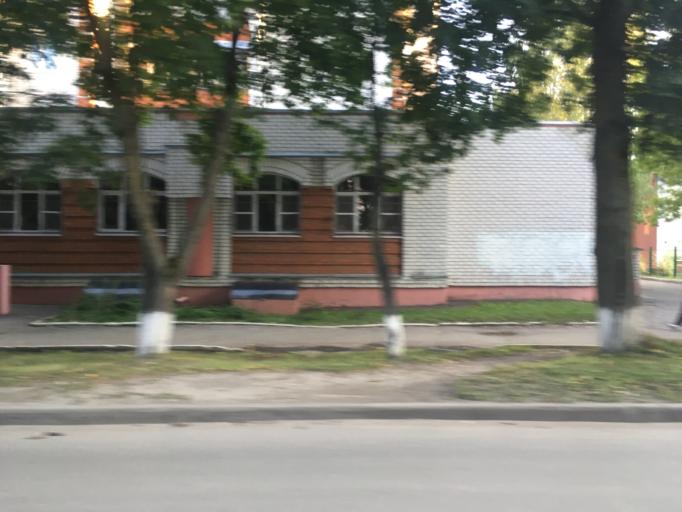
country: RU
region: Mariy-El
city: Yoshkar-Ola
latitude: 56.6482
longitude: 47.8795
